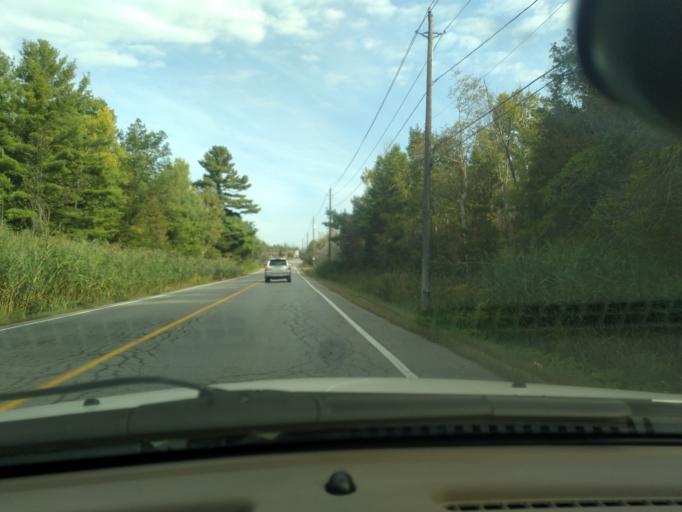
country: CA
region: Ontario
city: Innisfil
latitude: 44.3439
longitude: -79.6631
